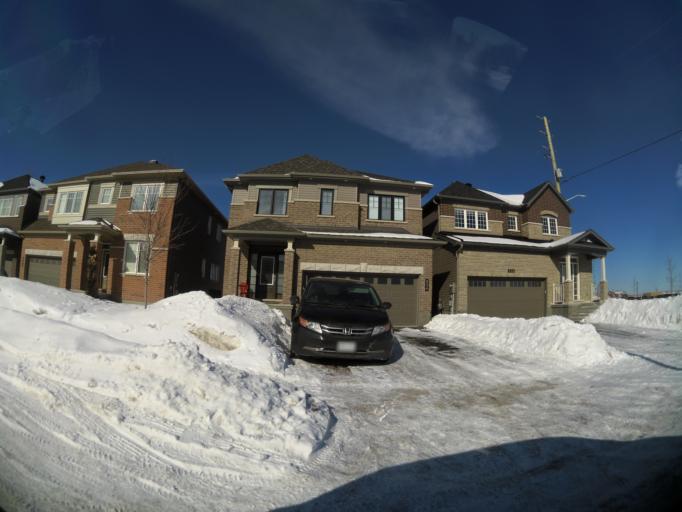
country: CA
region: Ontario
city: Ottawa
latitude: 45.4359
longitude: -75.5066
